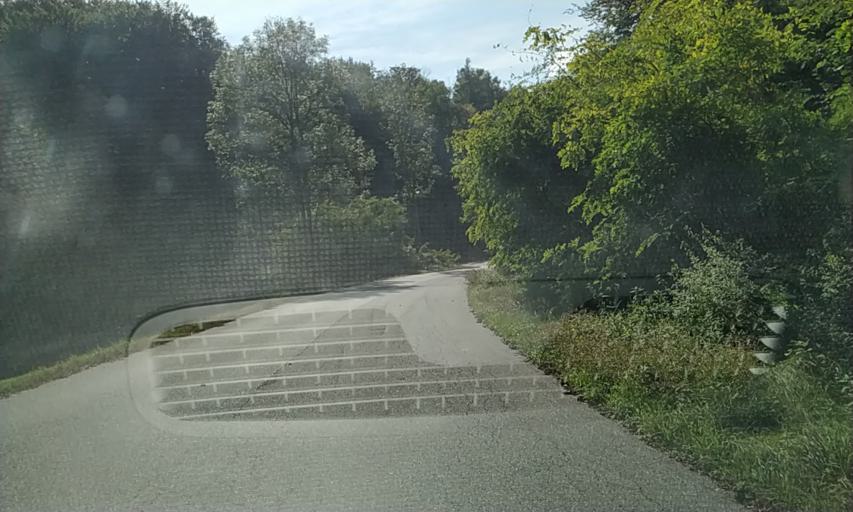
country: IT
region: Piedmont
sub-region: Provincia di Biella
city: Portula
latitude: 45.6776
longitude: 8.1775
